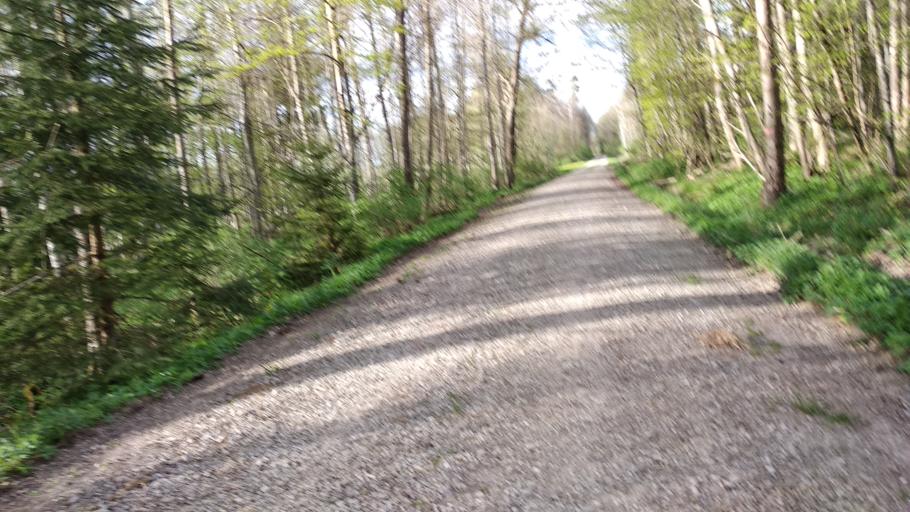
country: DE
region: Bavaria
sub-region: Swabia
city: Woringen
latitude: 47.9315
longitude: 10.1884
